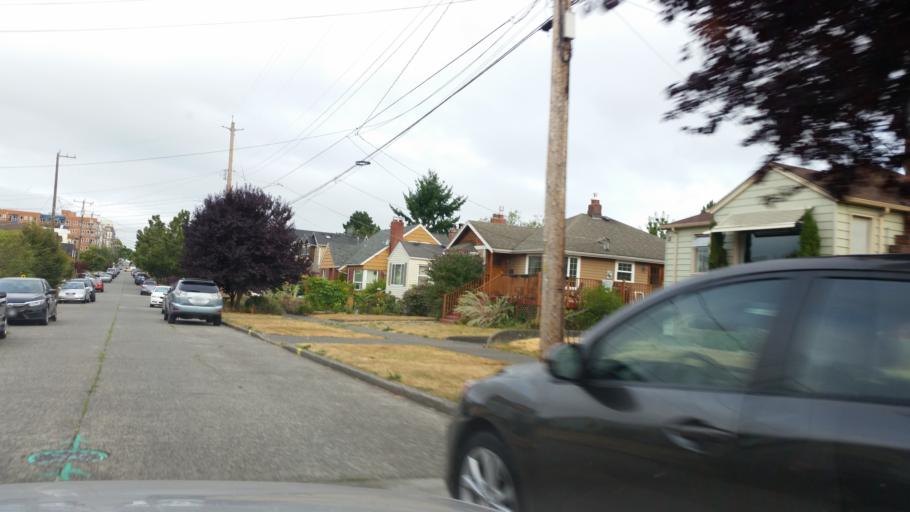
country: US
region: Washington
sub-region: King County
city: Seattle
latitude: 47.6695
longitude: -122.3697
